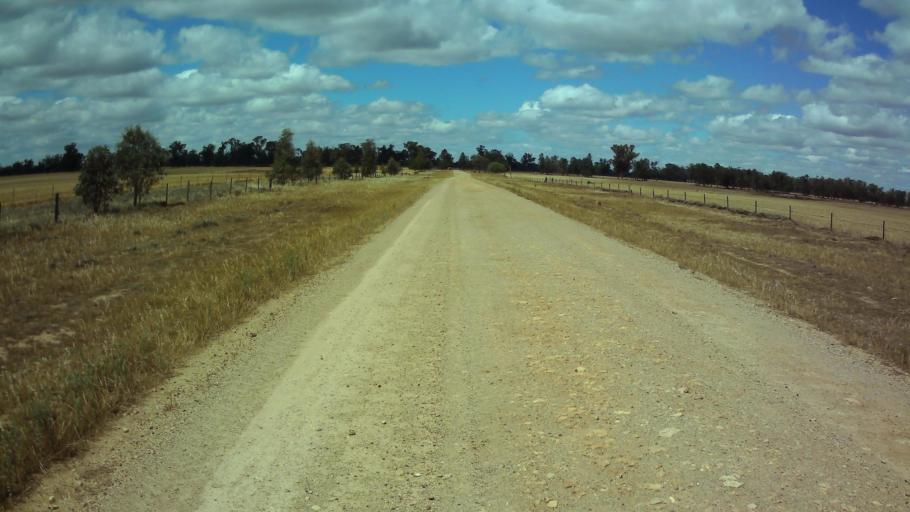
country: AU
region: New South Wales
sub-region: Weddin
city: Grenfell
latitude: -34.0110
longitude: 147.9163
